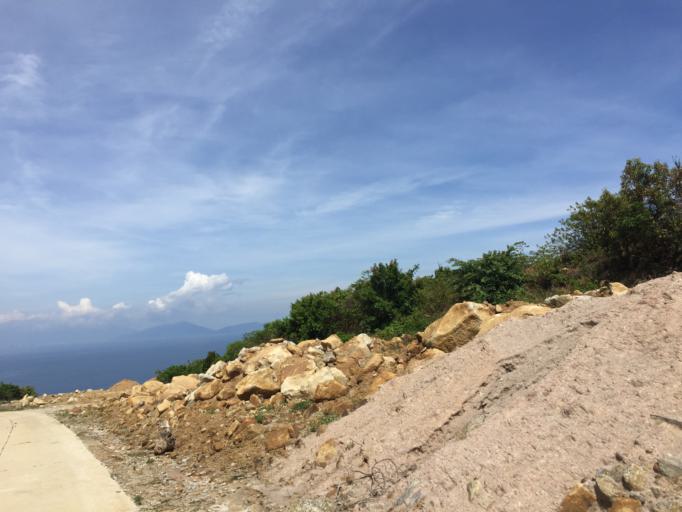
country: VN
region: Quang Nam
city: Hoi An
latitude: 15.9760
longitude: 108.5040
